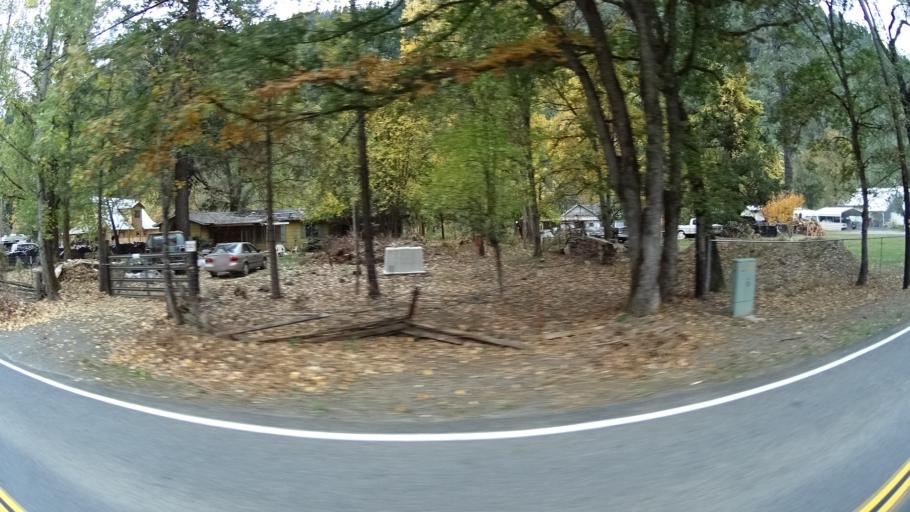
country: US
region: California
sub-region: Siskiyou County
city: Happy Camp
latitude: 41.8296
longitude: -123.3837
